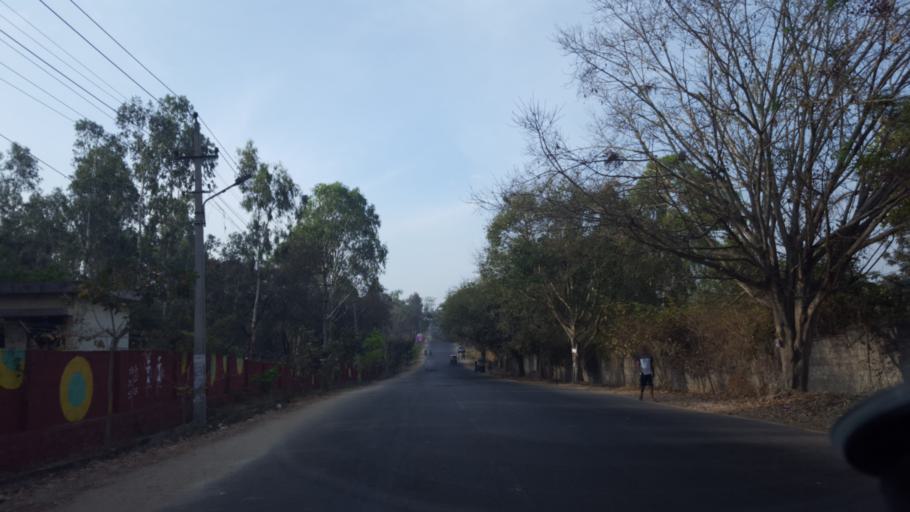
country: IN
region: Karnataka
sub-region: Bangalore Urban
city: Bangalore
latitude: 12.9103
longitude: 77.5000
